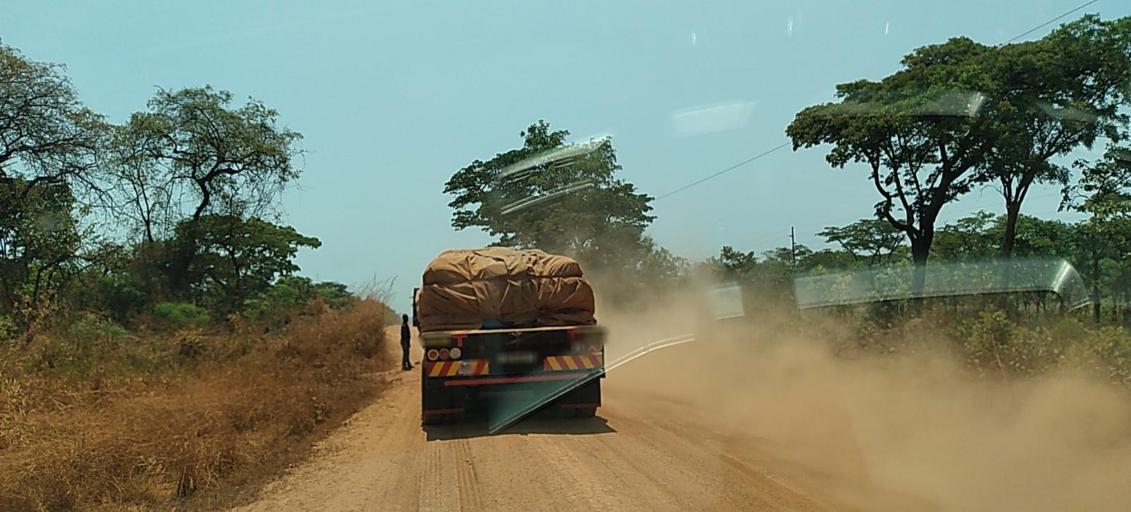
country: CD
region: Katanga
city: Kipushi
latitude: -11.9266
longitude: 26.9991
